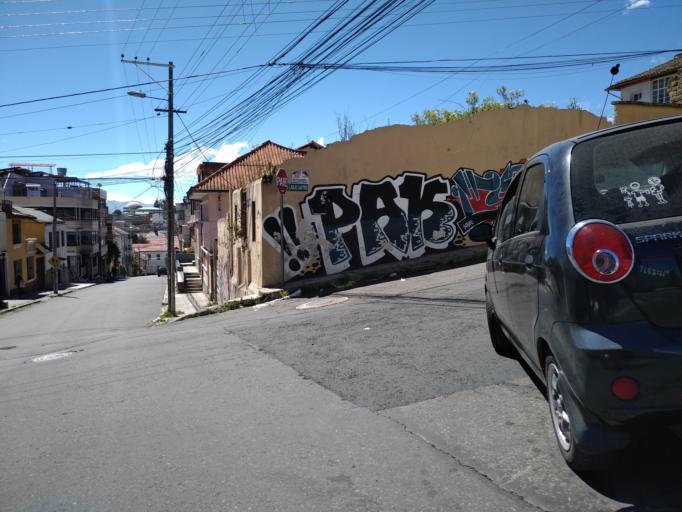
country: EC
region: Pichincha
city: Quito
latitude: -0.2173
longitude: -78.5015
